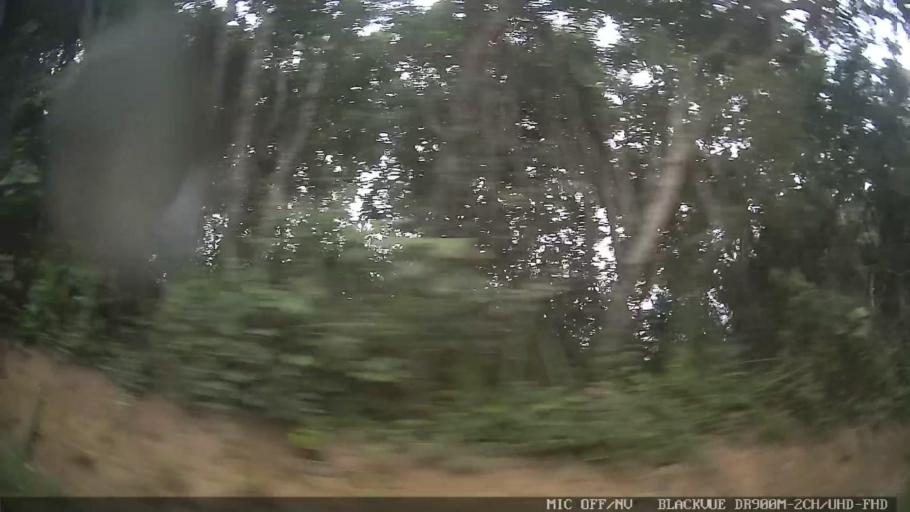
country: BR
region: Sao Paulo
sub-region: Suzano
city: Suzano
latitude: -23.6807
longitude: -46.2370
